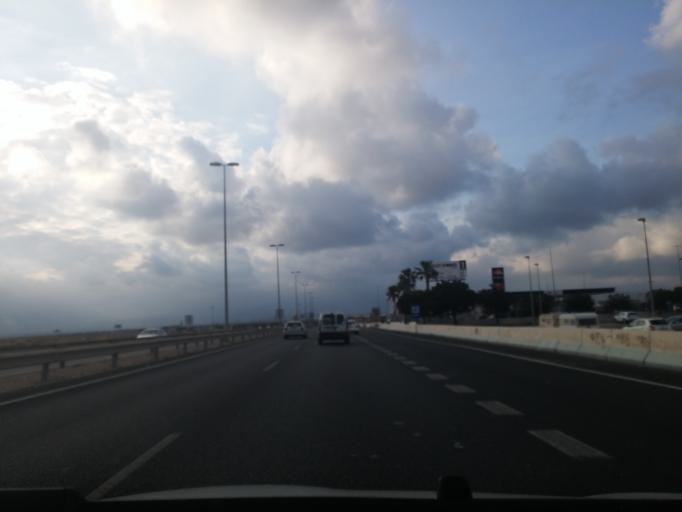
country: ES
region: Valencia
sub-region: Provincia de Alicante
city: San Vicent del Raspeig
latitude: 38.3750
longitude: -0.5083
